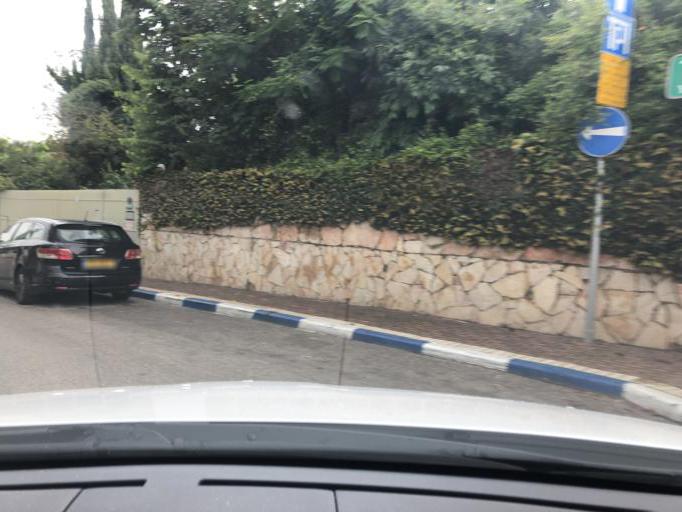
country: IL
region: Tel Aviv
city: Giv`atayim
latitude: 32.0571
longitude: 34.8204
